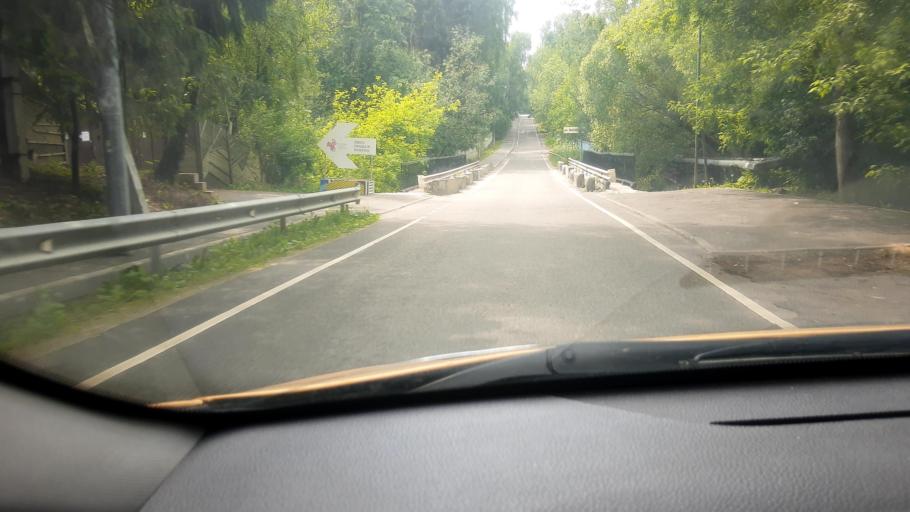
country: RU
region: Moskovskaya
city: Vatutinki
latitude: 55.5039
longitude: 37.3197
